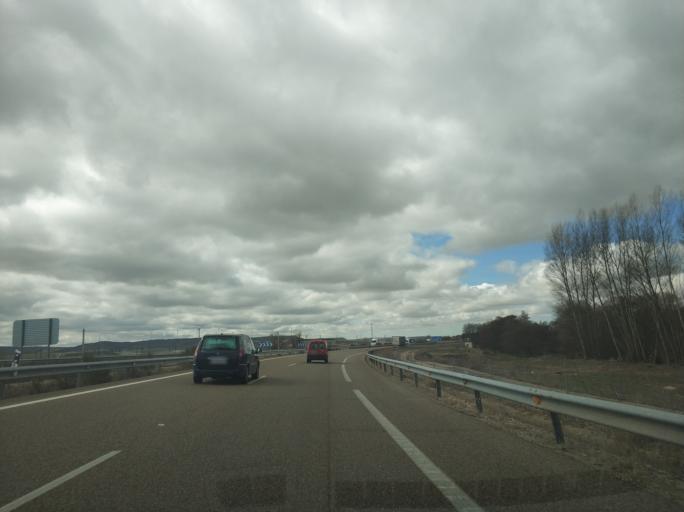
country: ES
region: Castille and Leon
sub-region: Provincia de Palencia
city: Cordovilla la Real
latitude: 42.0577
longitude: -4.2368
